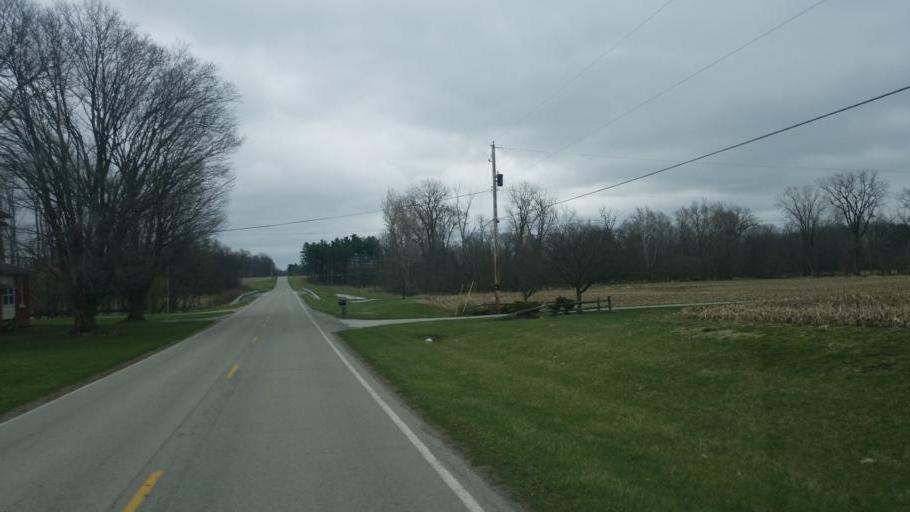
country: US
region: Ohio
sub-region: Wyandot County
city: Upper Sandusky
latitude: 40.8262
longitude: -83.1549
